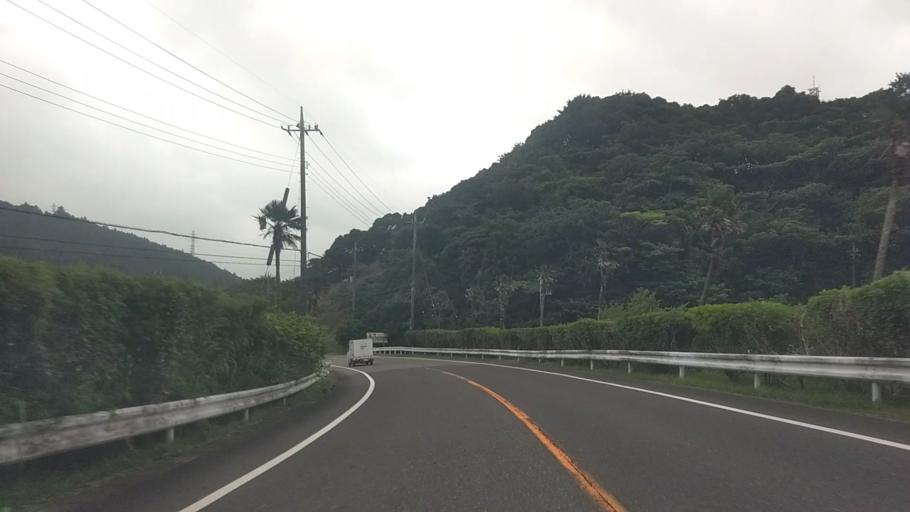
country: JP
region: Chiba
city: Kawaguchi
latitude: 35.1460
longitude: 140.0685
